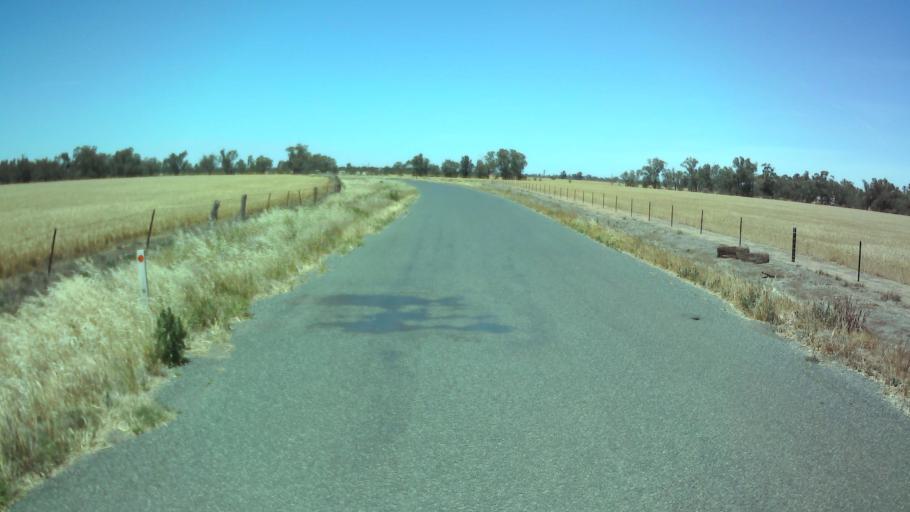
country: AU
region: New South Wales
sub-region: Weddin
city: Grenfell
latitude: -34.0347
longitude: 147.7898
